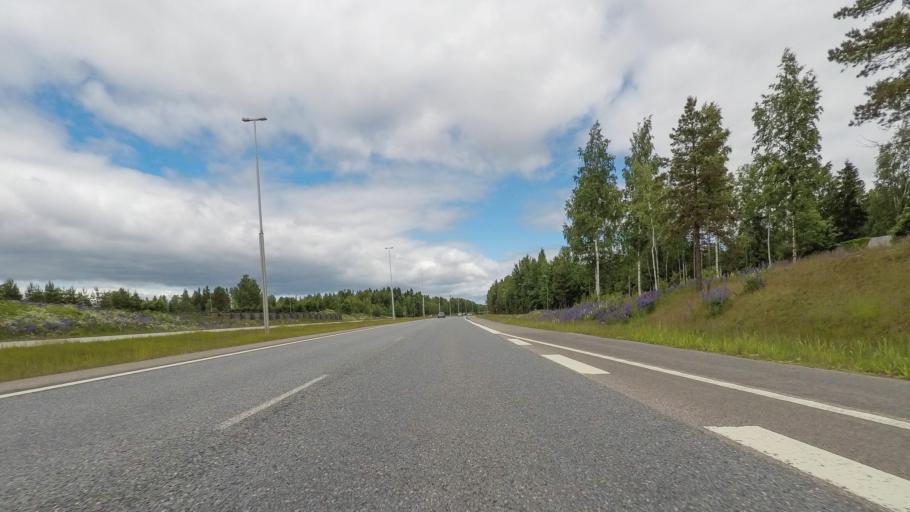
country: FI
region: Uusimaa
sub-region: Helsinki
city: Kerava
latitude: 60.3460
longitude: 25.1104
